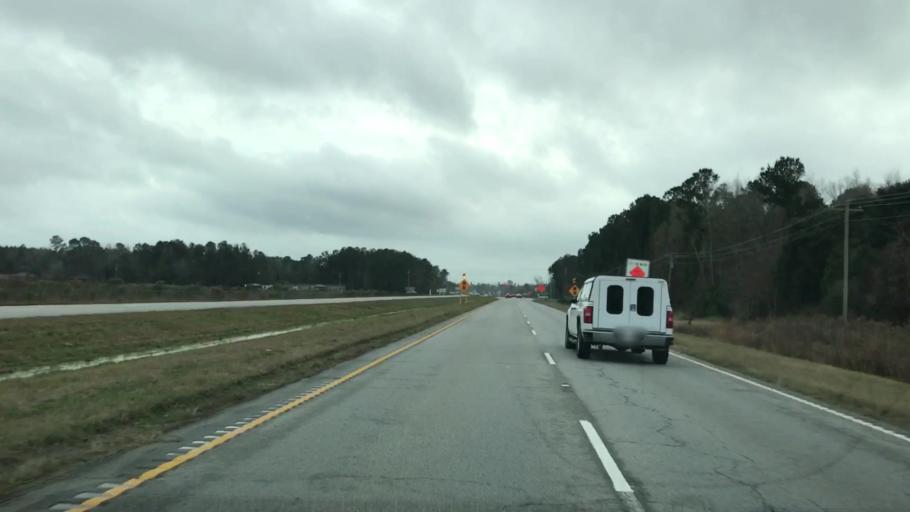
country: US
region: South Carolina
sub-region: Berkeley County
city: Moncks Corner
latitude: 33.1511
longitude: -80.0329
